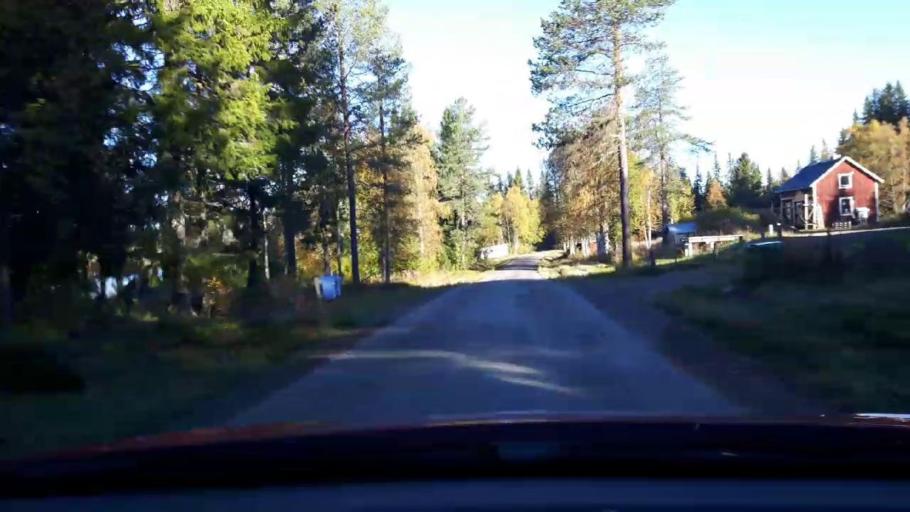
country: SE
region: Jaemtland
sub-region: Stroemsunds Kommun
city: Stroemsund
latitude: 64.3978
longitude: 15.1450
